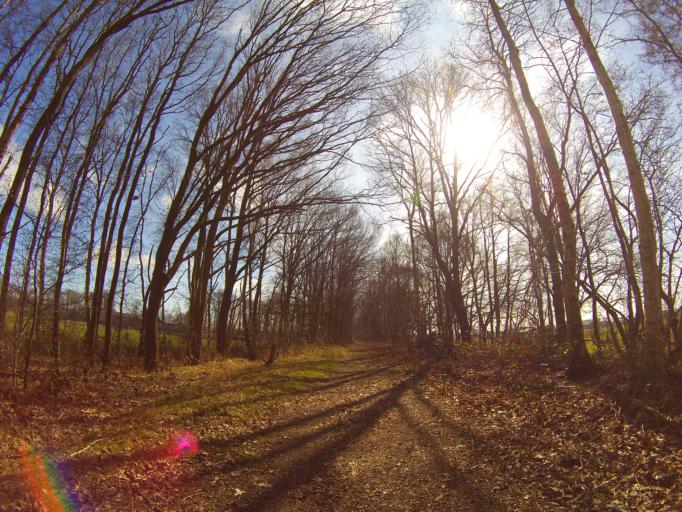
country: NL
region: Utrecht
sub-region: Gemeente Utrechtse Heuvelrug
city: Overberg
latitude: 52.0691
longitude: 5.4605
